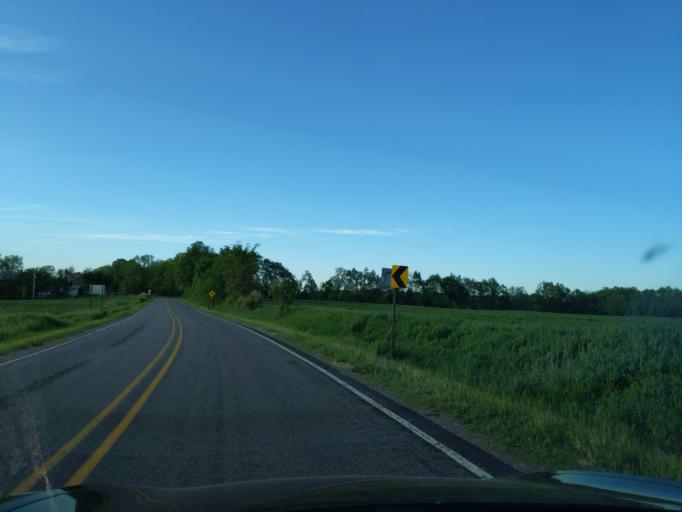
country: US
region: Michigan
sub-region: Ingham County
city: Leslie
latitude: 42.4440
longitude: -84.3136
